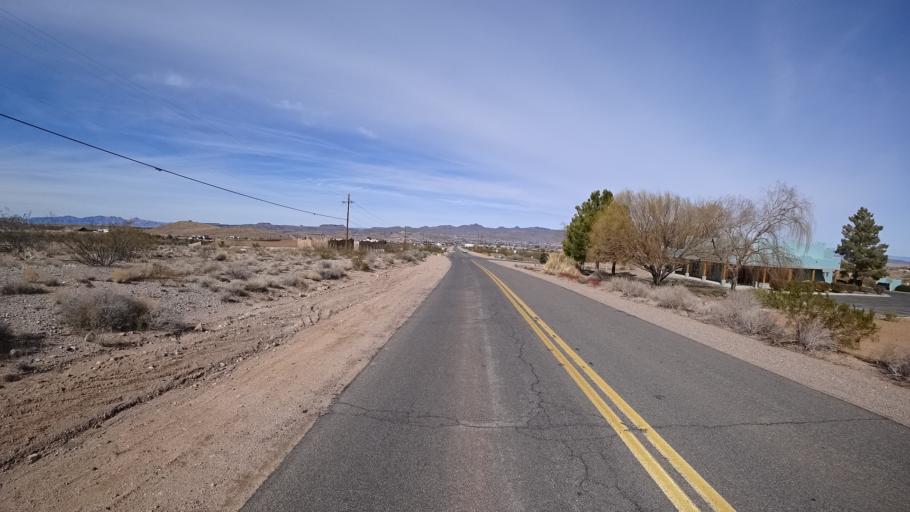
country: US
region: Arizona
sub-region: Mohave County
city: Kingman
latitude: 35.1797
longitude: -113.9943
